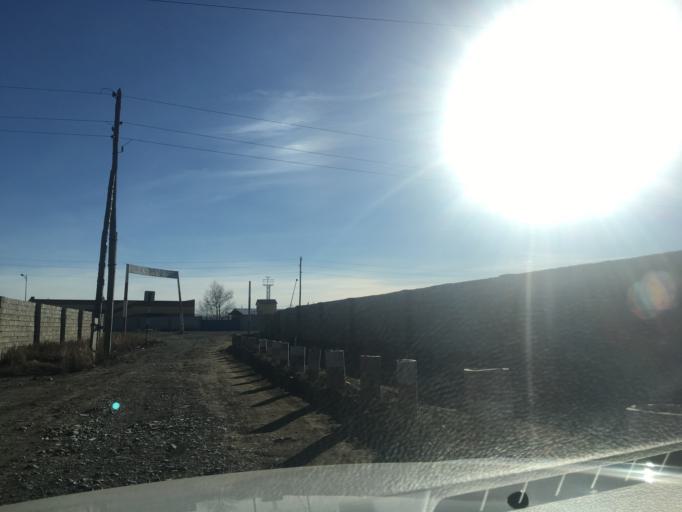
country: MN
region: Ulaanbaatar
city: Ulaanbaatar
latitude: 47.9026
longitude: 106.7763
